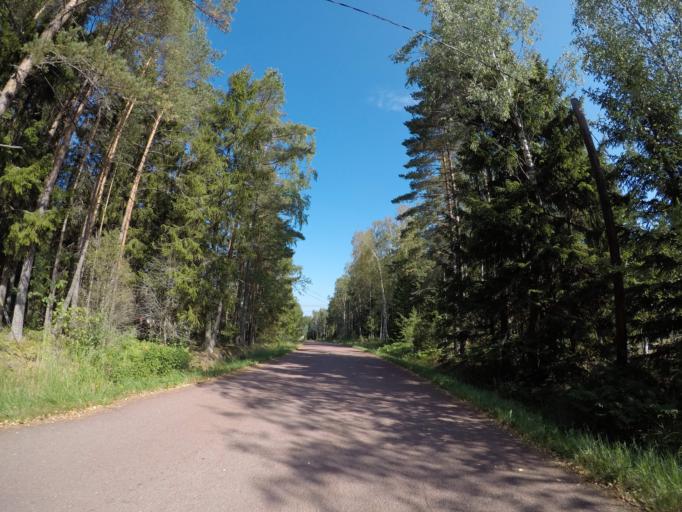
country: AX
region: Alands landsbygd
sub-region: Finstroem
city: Finstroem
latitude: 60.2803
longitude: 19.9171
